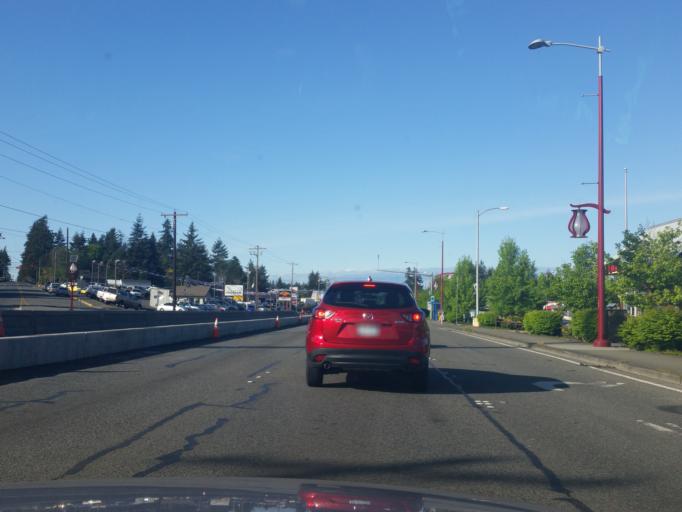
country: US
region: Washington
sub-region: Snohomish County
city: Esperance
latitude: 47.7942
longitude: -122.3356
